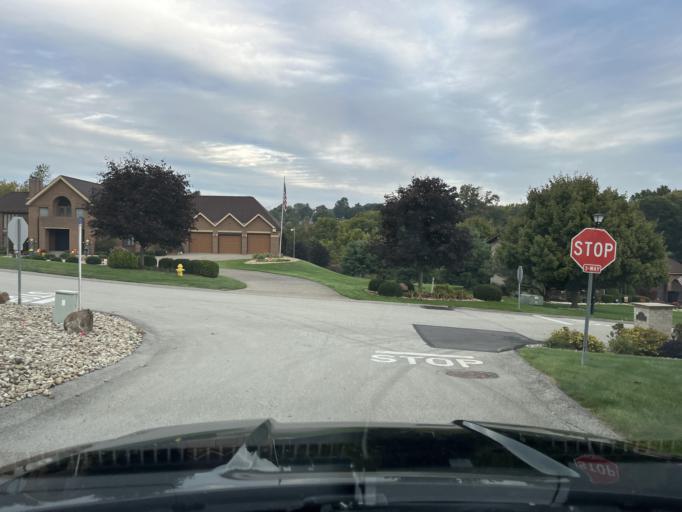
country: US
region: Pennsylvania
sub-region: Fayette County
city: Leith-Hatfield
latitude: 39.8719
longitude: -79.7262
